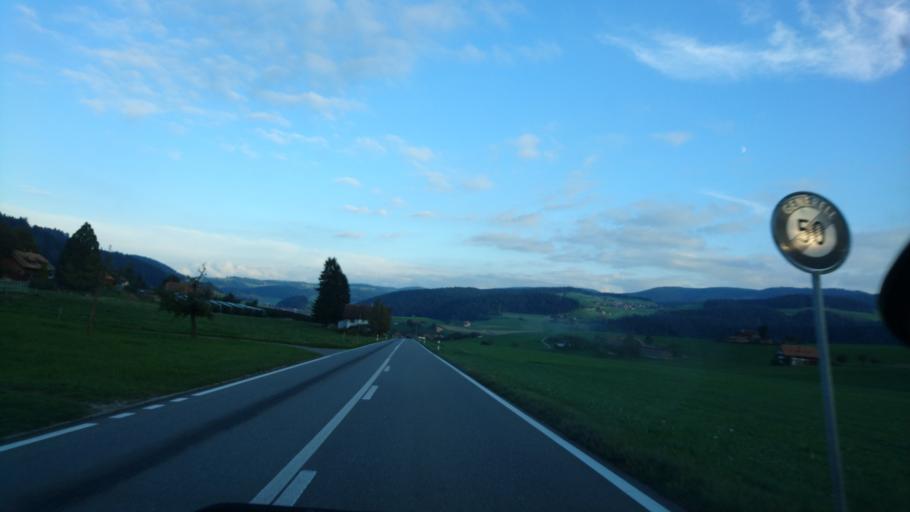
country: CH
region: Bern
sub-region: Bern-Mittelland District
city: Zaziwil
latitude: 46.9038
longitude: 7.6453
